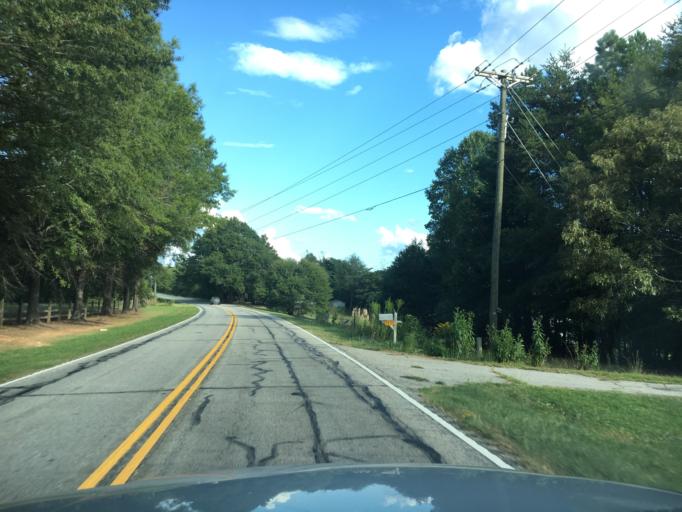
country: US
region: South Carolina
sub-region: Laurens County
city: Laurens
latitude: 34.5194
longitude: -82.1106
